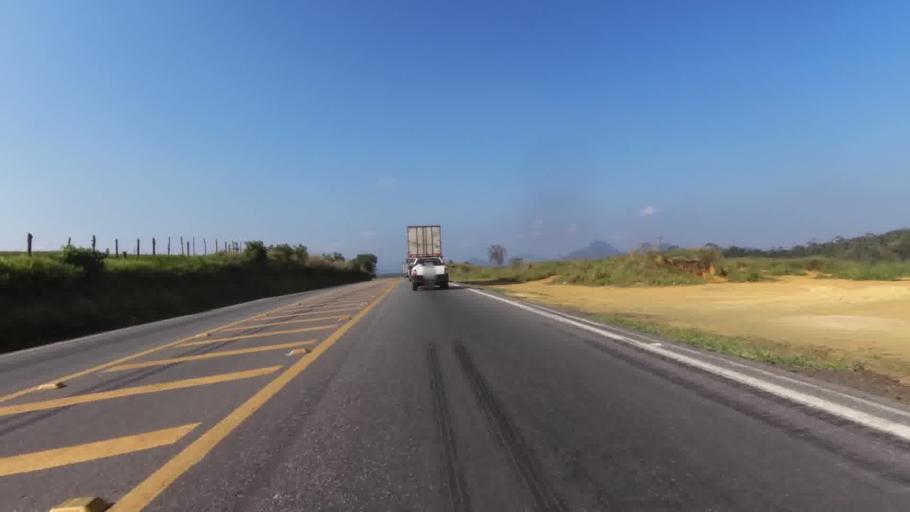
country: BR
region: Espirito Santo
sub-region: Alfredo Chaves
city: Alfredo Chaves
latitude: -20.6963
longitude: -40.7097
